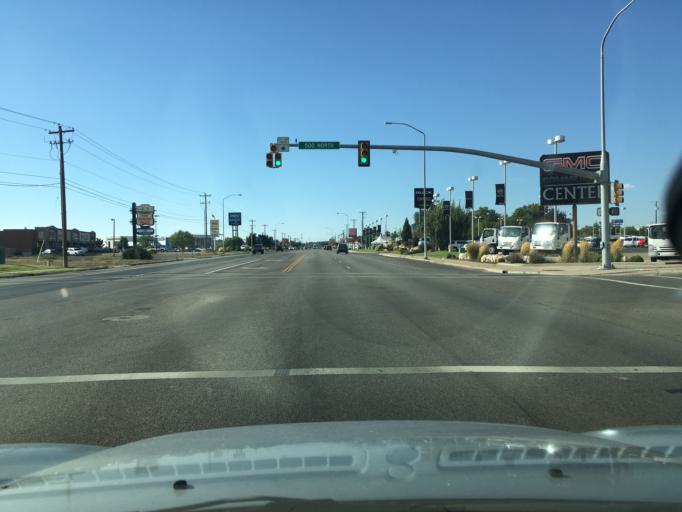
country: US
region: Utah
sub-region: Davis County
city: Layton
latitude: 41.0672
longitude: -111.9729
